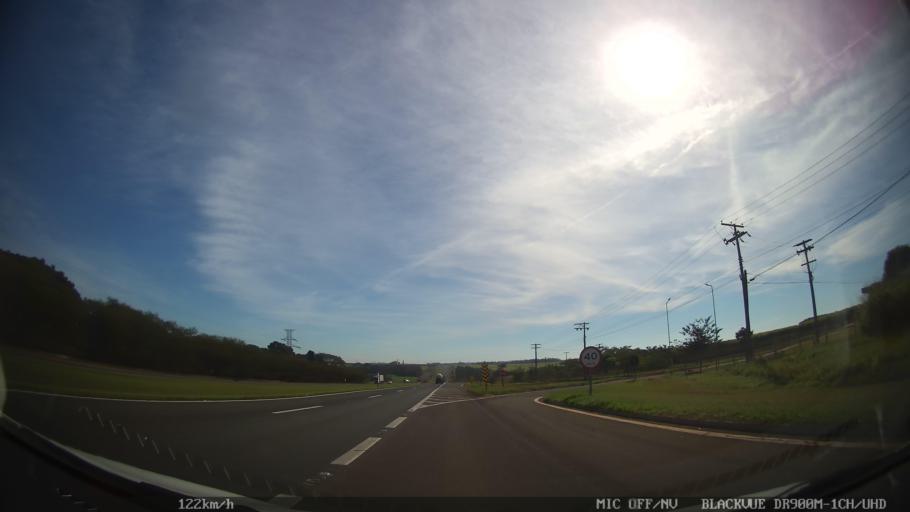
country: BR
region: Sao Paulo
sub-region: Araras
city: Araras
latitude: -22.3165
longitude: -47.3904
